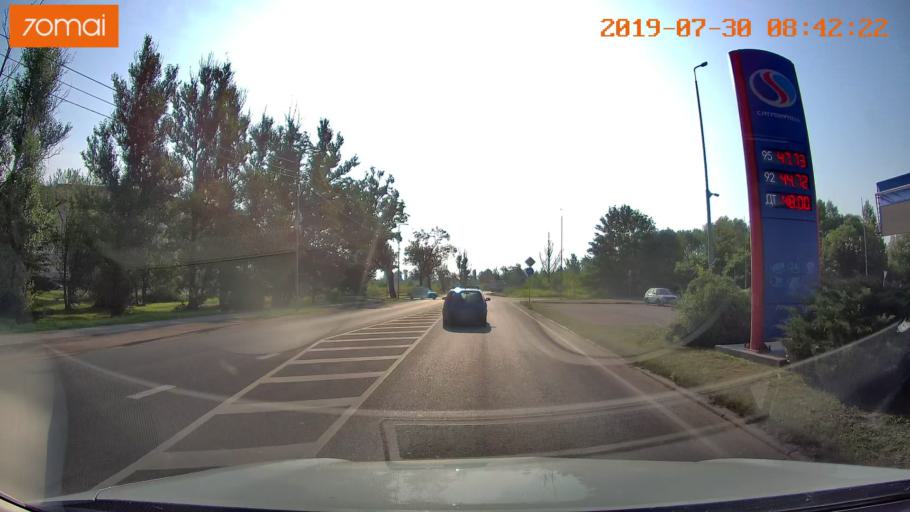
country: RU
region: Kaliningrad
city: Chernyakhovsk
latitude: 54.6296
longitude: 21.8271
